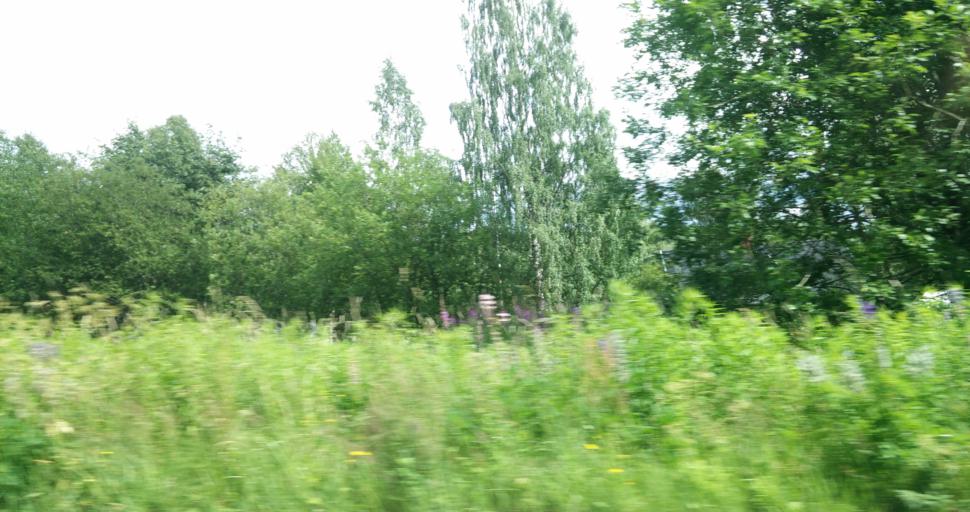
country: SE
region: Vaermland
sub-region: Hagfors Kommun
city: Hagfors
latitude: 60.0318
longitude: 13.6261
